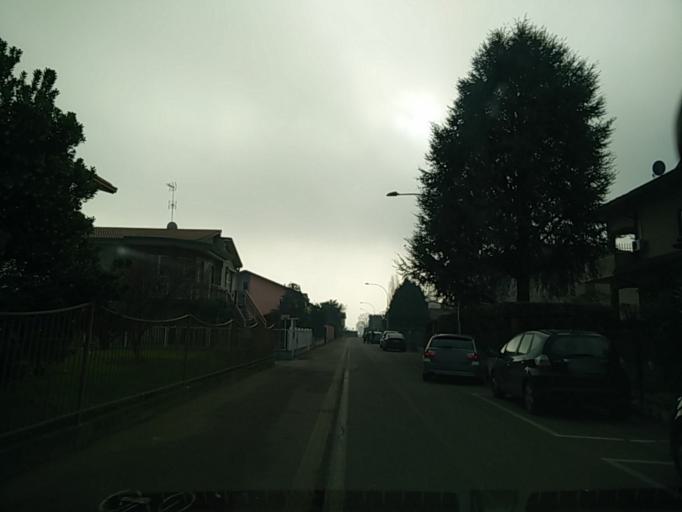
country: IT
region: Lombardy
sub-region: Provincia di Pavia
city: Rotta
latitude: 45.1623
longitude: 9.1465
